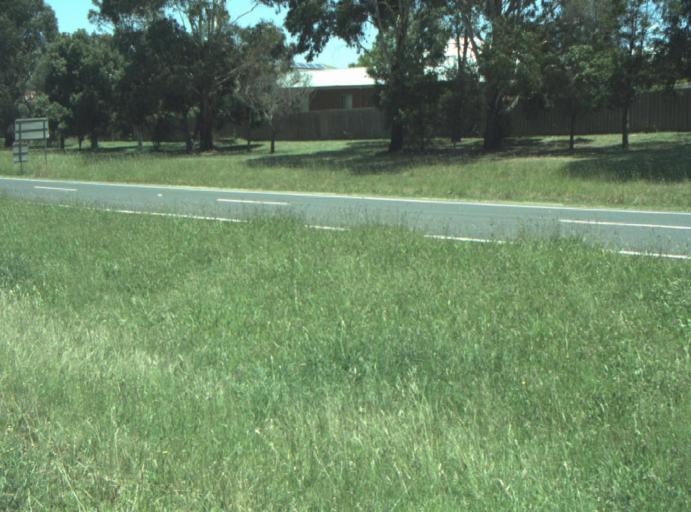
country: AU
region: Victoria
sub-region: Greater Geelong
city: Wandana Heights
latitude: -38.1943
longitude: 144.3223
